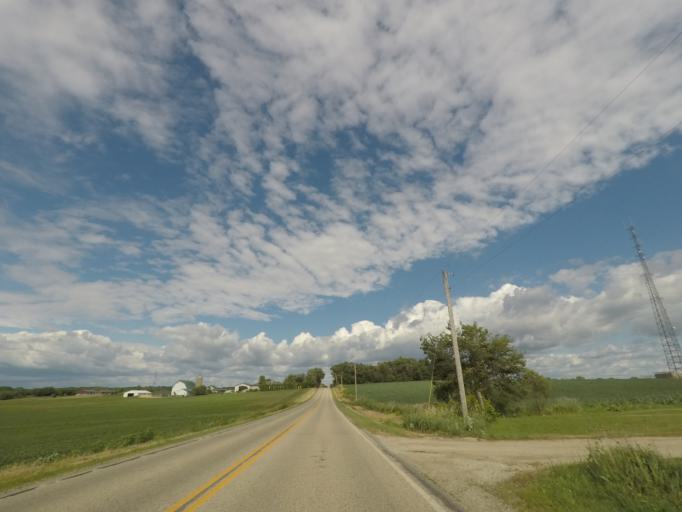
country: US
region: Wisconsin
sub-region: Rock County
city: Janesville
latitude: 42.7012
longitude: -89.0960
